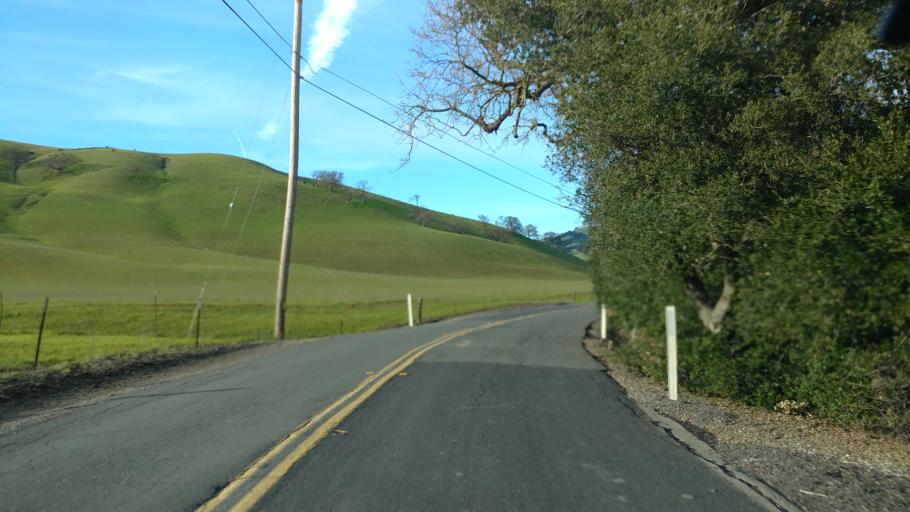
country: US
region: California
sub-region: Contra Costa County
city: Blackhawk
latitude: 37.8103
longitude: -121.8585
